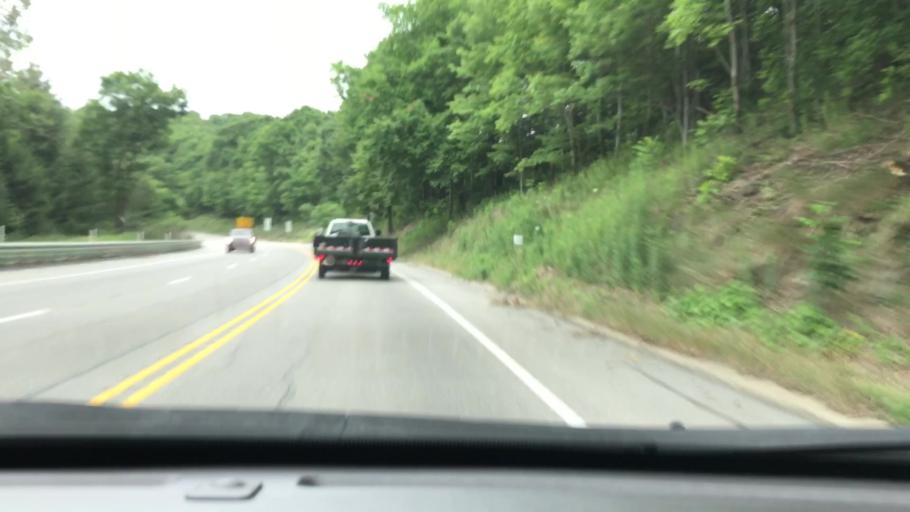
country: US
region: Pennsylvania
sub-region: Elk County
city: Ridgway
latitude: 41.4180
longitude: -78.7152
